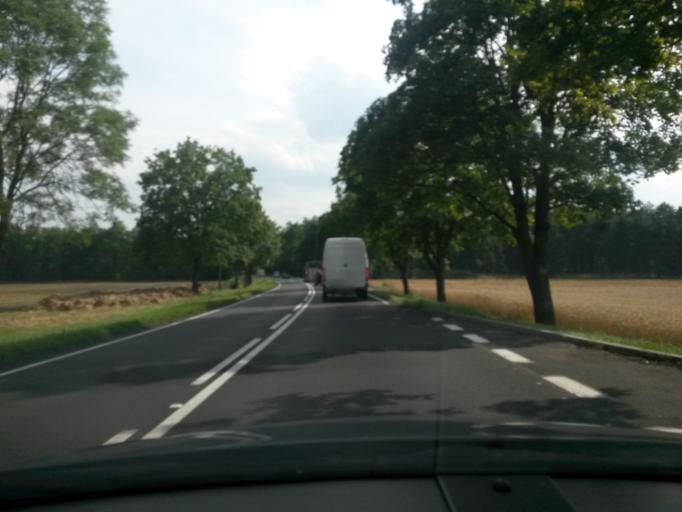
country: PL
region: Greater Poland Voivodeship
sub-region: Powiat sremski
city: Srem
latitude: 52.1546
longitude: 17.0350
